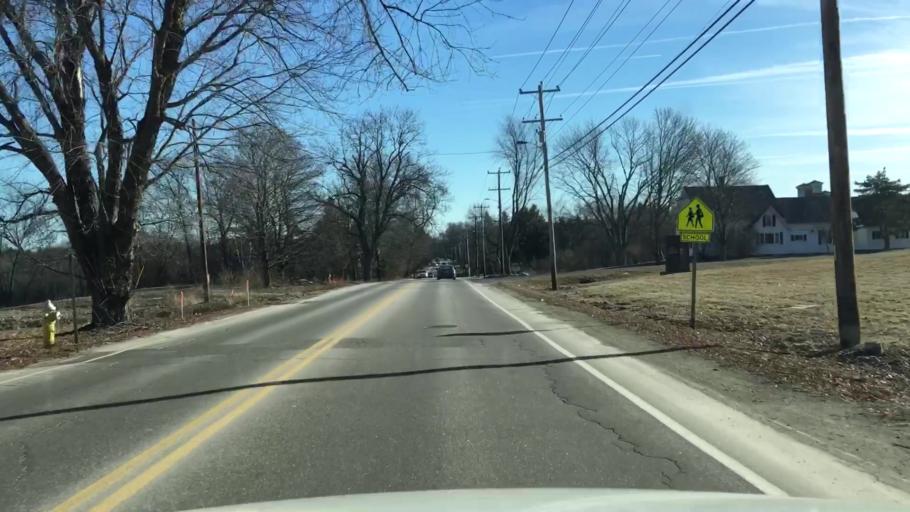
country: US
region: Maine
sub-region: Penobscot County
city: Bangor
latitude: 44.8182
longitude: -68.8013
